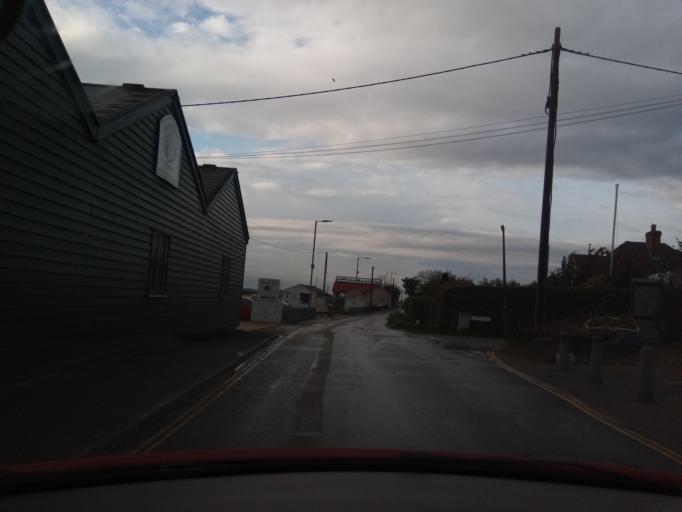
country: GB
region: England
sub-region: Essex
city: West Mersea
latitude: 51.7767
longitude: 0.9006
